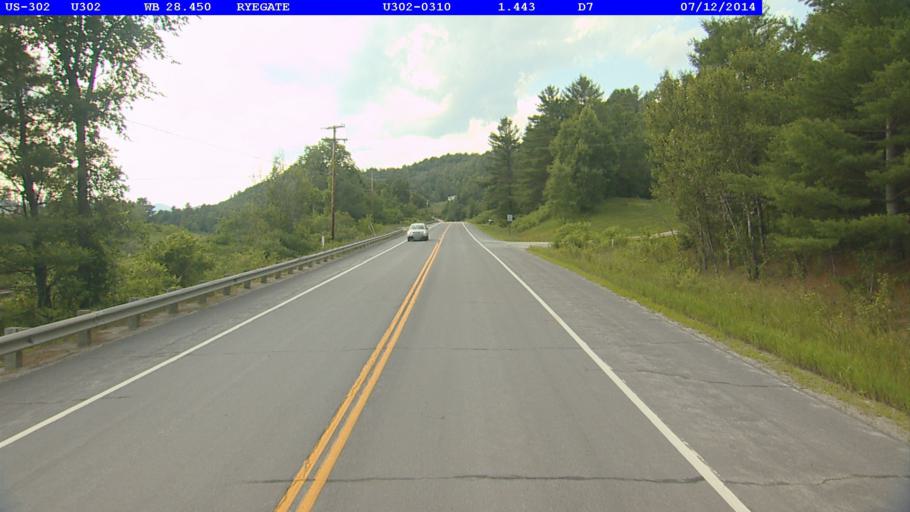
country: US
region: New Hampshire
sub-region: Grafton County
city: Woodsville
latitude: 44.1936
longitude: -72.1482
